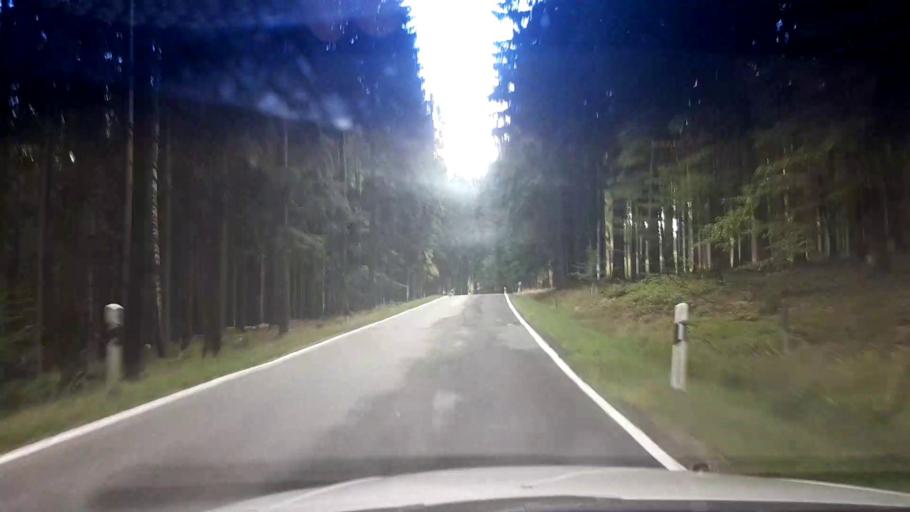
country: DE
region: Bavaria
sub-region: Upper Palatinate
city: Neualbenreuth
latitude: 49.9387
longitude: 12.4095
